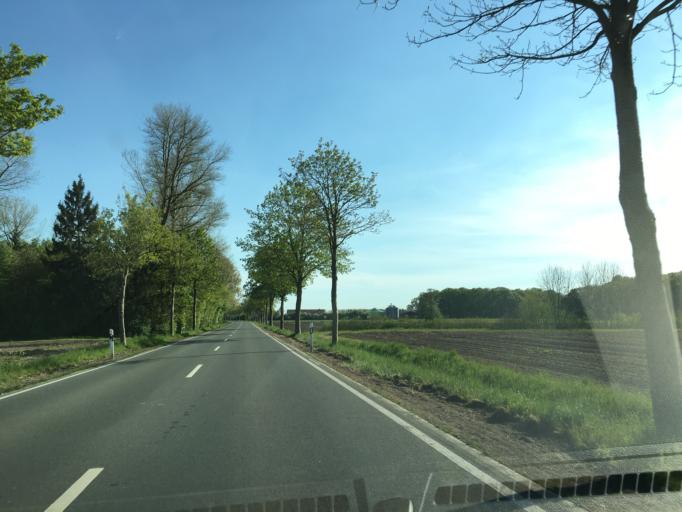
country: DE
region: North Rhine-Westphalia
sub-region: Regierungsbezirk Munster
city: Senden
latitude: 51.8086
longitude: 7.5373
